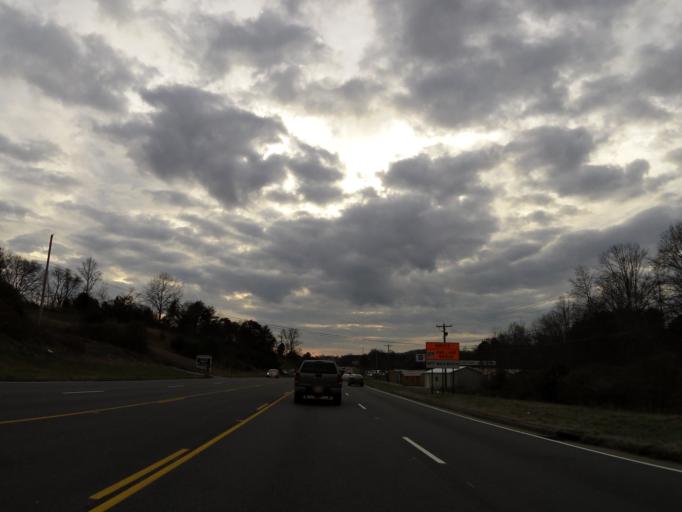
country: US
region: Tennessee
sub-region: Blount County
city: Maryville
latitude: 35.7025
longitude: -84.0375
